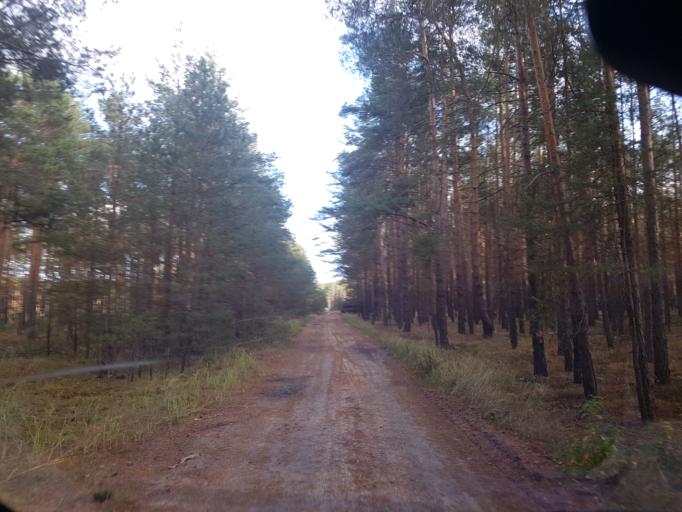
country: DE
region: Brandenburg
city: Finsterwalde
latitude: 51.5558
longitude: 13.6798
